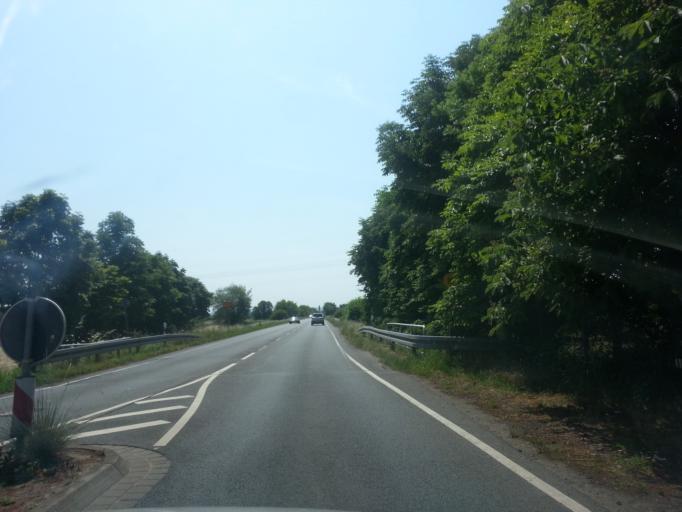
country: DE
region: Hesse
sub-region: Regierungsbezirk Darmstadt
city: Eppertshausen
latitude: 49.9438
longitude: 8.8494
